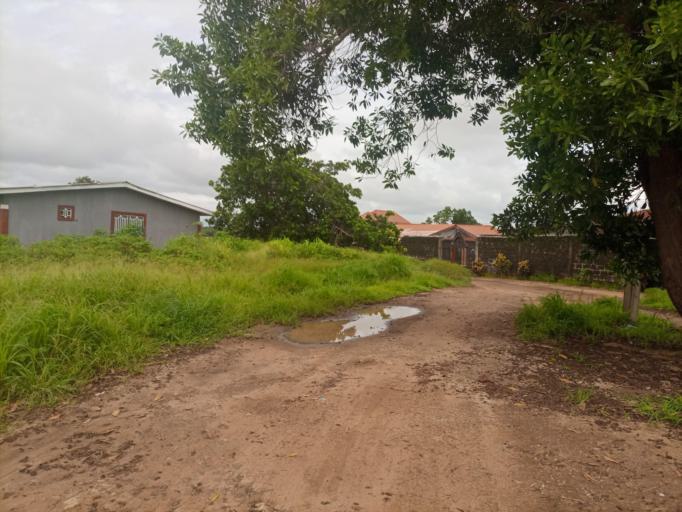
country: SL
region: Northern Province
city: Masoyila
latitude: 8.5965
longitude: -13.1767
